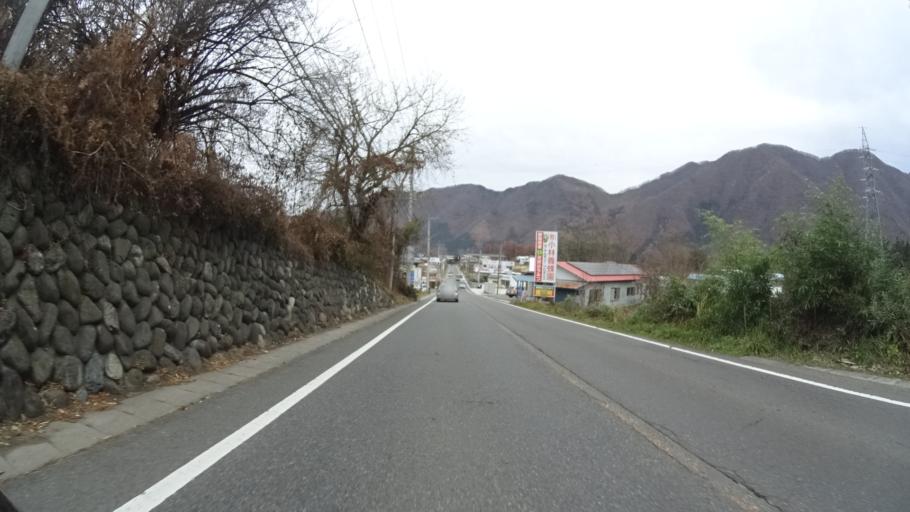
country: JP
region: Gunma
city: Numata
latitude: 36.6733
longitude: 139.1991
